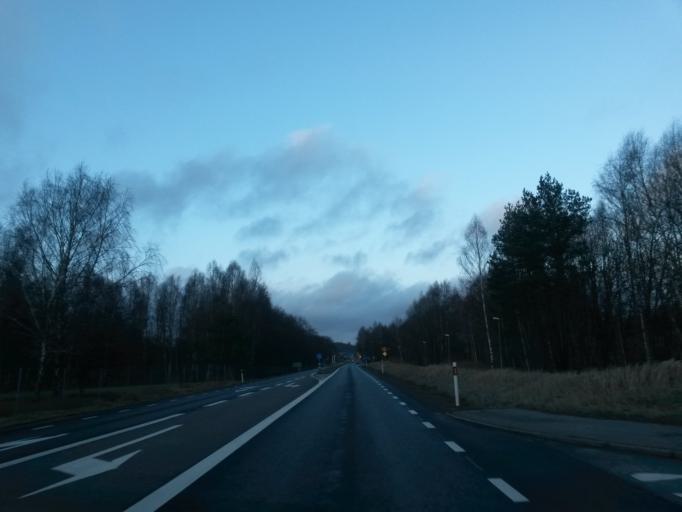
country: SE
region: Halland
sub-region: Halmstads Kommun
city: Oskarstrom
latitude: 56.8001
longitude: 12.9592
